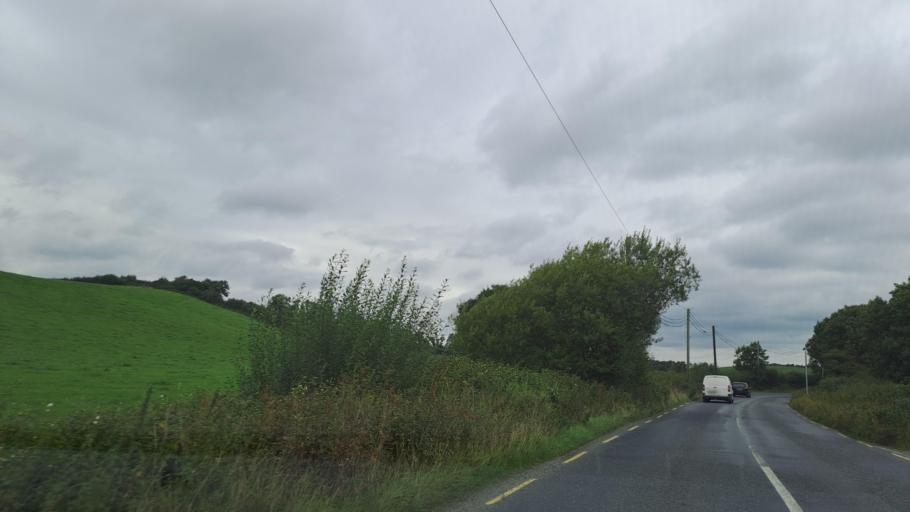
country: IE
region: Ulster
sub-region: An Cabhan
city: Bailieborough
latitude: 53.9732
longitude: -6.9134
